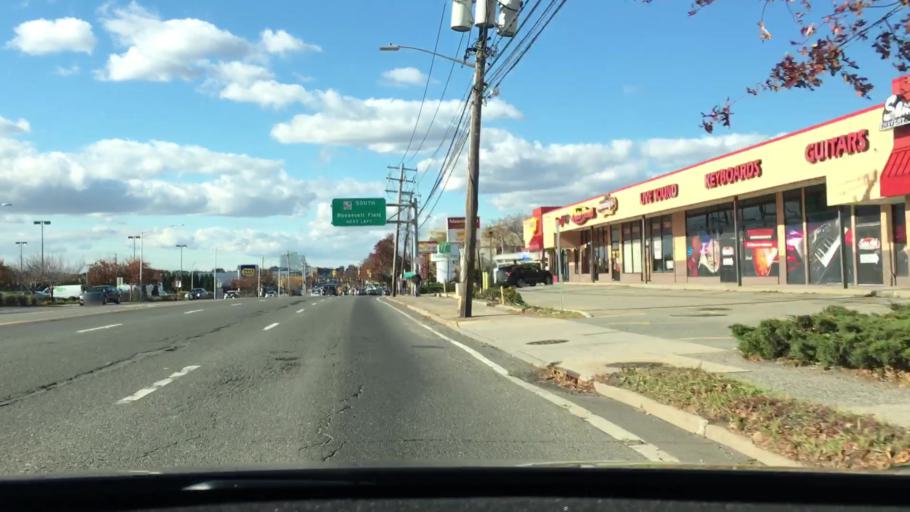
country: US
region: New York
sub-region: Nassau County
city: Carle Place
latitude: 40.7457
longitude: -73.6009
